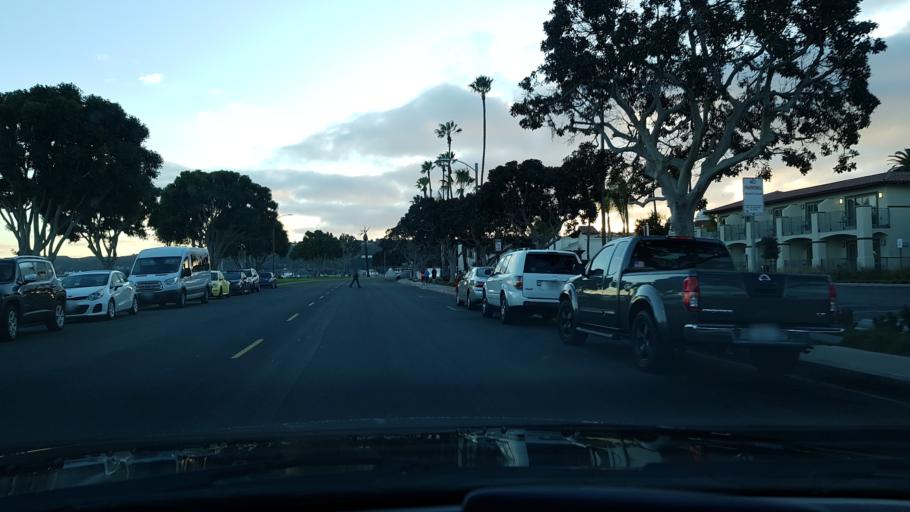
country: US
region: California
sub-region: San Diego County
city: Coronado
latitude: 32.7103
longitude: -117.2304
